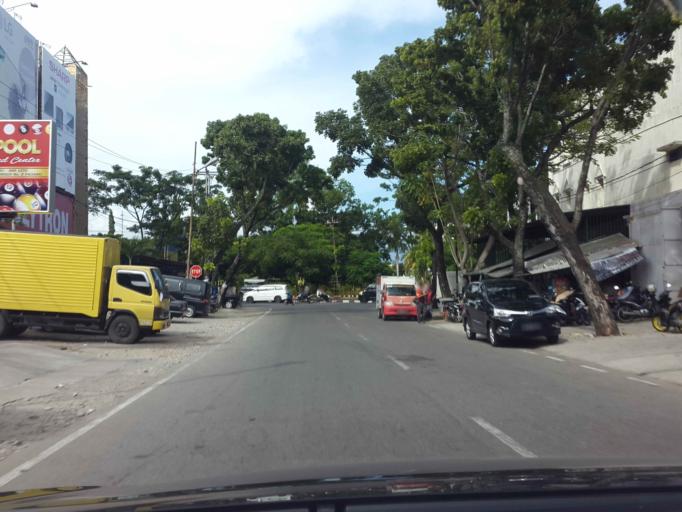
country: ID
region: West Sumatra
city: Padang
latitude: -0.9569
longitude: 100.3546
